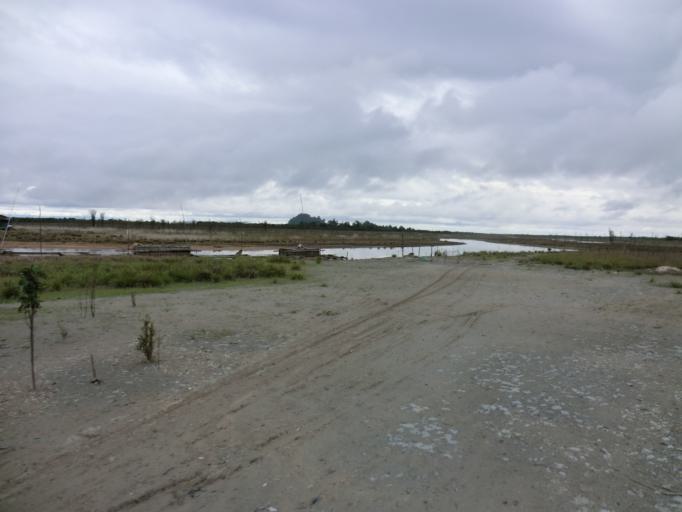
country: MY
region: Sarawak
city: Simanggang
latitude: 1.0130
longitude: 112.2147
